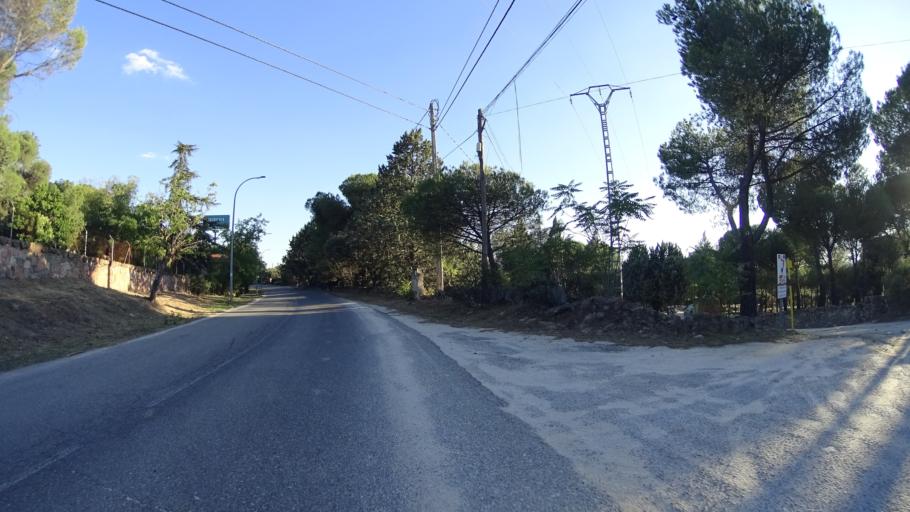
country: ES
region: Madrid
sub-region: Provincia de Madrid
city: Torrelodones
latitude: 40.5907
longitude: -3.9551
